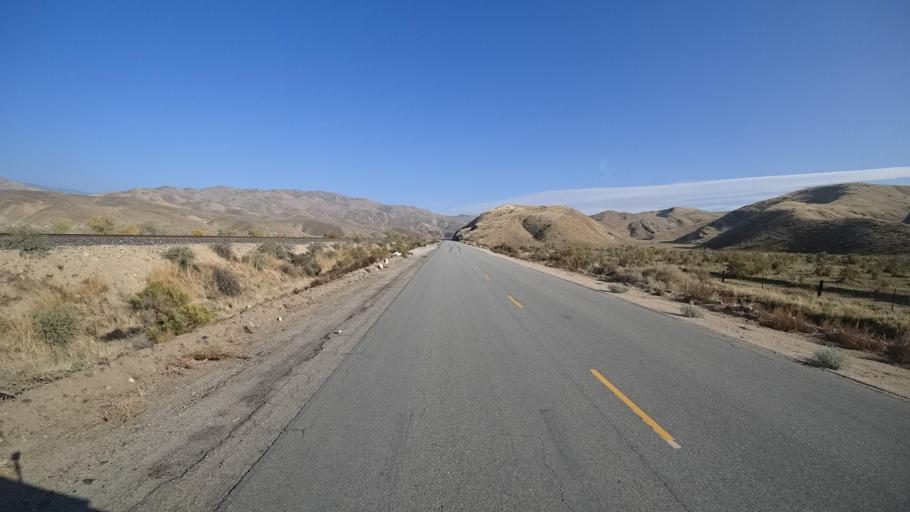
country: US
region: California
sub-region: Kern County
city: Arvin
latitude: 35.3242
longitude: -118.7213
